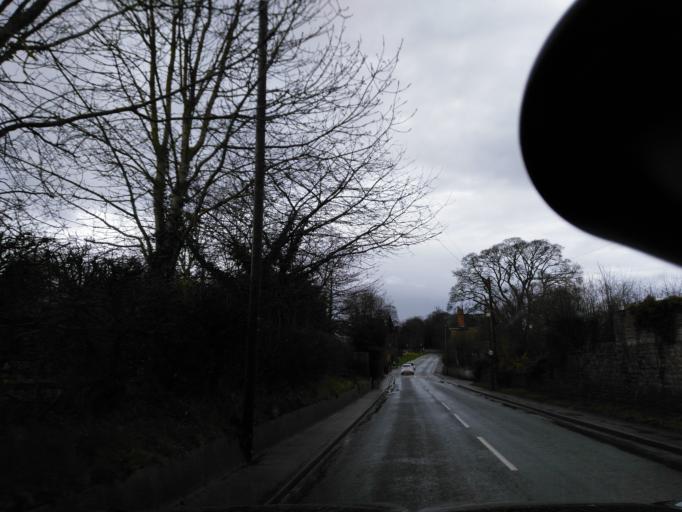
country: GB
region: England
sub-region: North Yorkshire
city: Ripon
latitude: 54.1427
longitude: -1.5034
